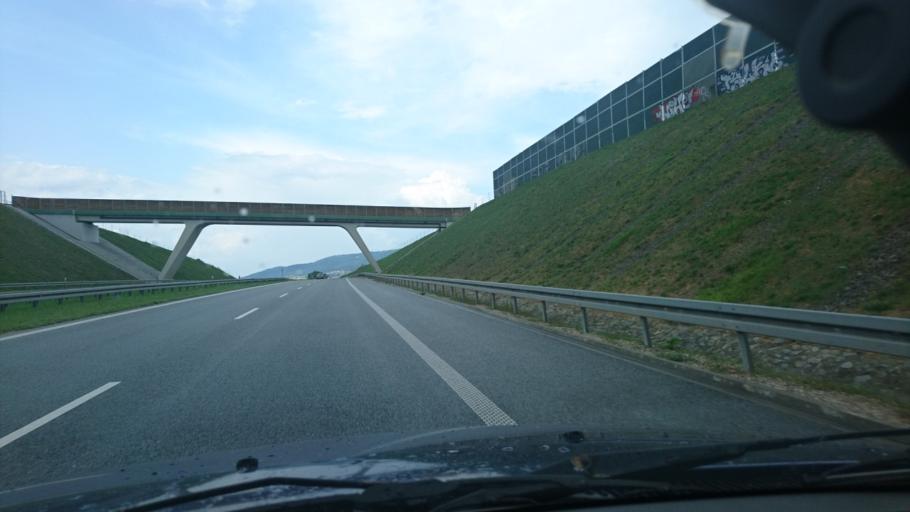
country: PL
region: Silesian Voivodeship
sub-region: Powiat zywiecki
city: Lesna
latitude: 49.6920
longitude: 19.1366
